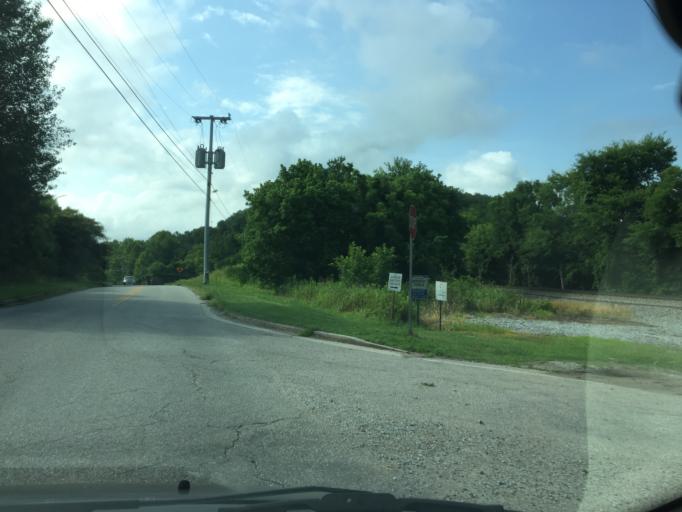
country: US
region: Tennessee
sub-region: Hamilton County
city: Apison
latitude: 35.0234
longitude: -85.0236
